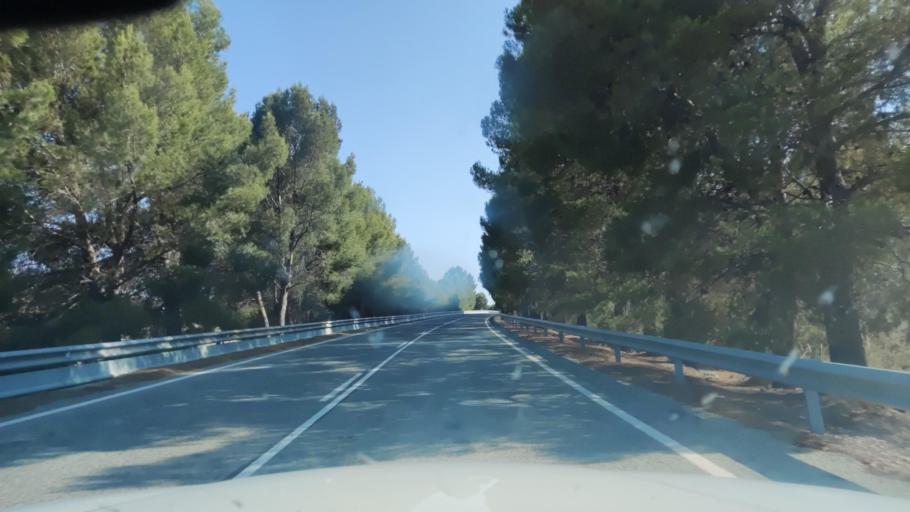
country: ES
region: Castille-La Mancha
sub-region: Provincia de Albacete
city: Tobarra
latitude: 38.6439
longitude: -1.6664
